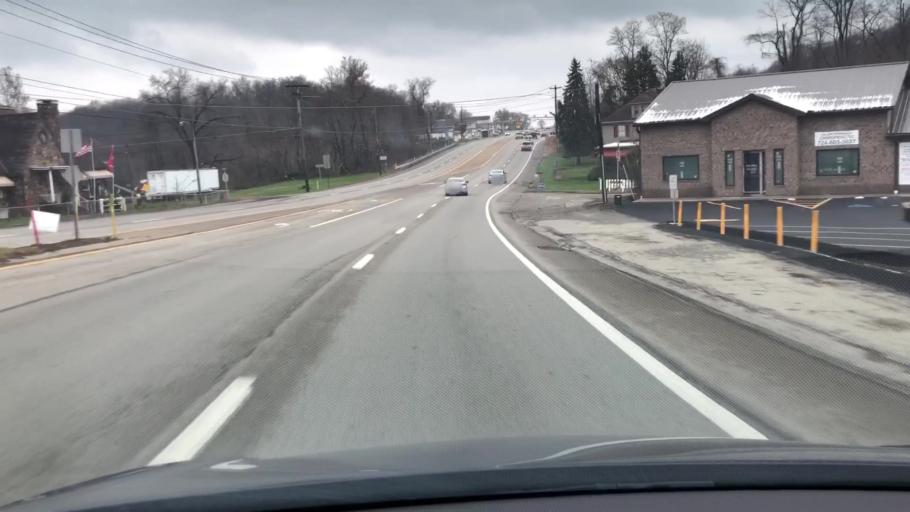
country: US
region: Pennsylvania
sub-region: Fayette County
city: South Connellsville
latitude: 40.0040
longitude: -79.6031
